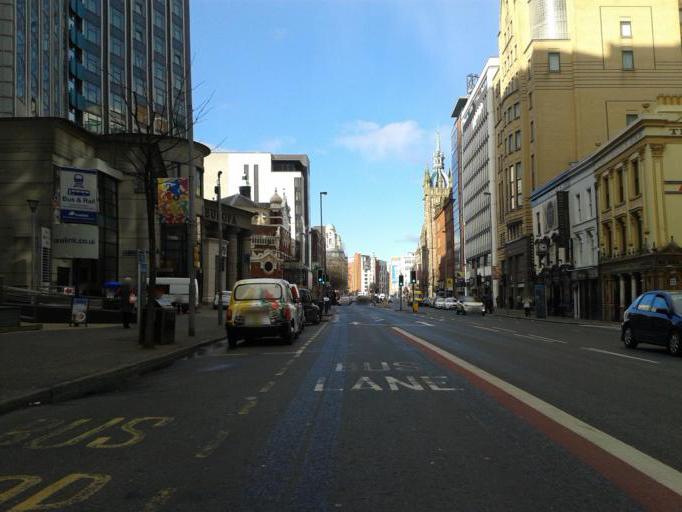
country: GB
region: Northern Ireland
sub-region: City of Belfast
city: Belfast
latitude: 54.5943
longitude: -5.9344
